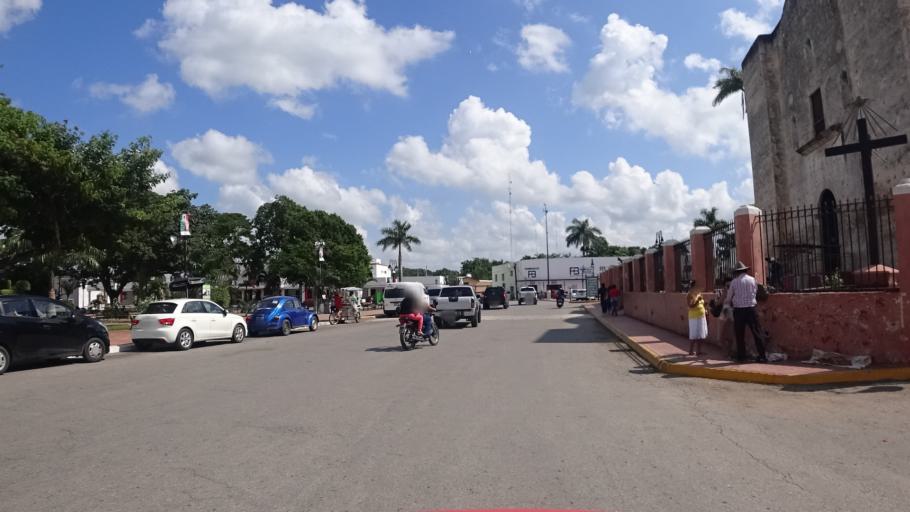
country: MX
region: Yucatan
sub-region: Tizimin
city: Tizimin
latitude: 21.1425
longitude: -88.1522
